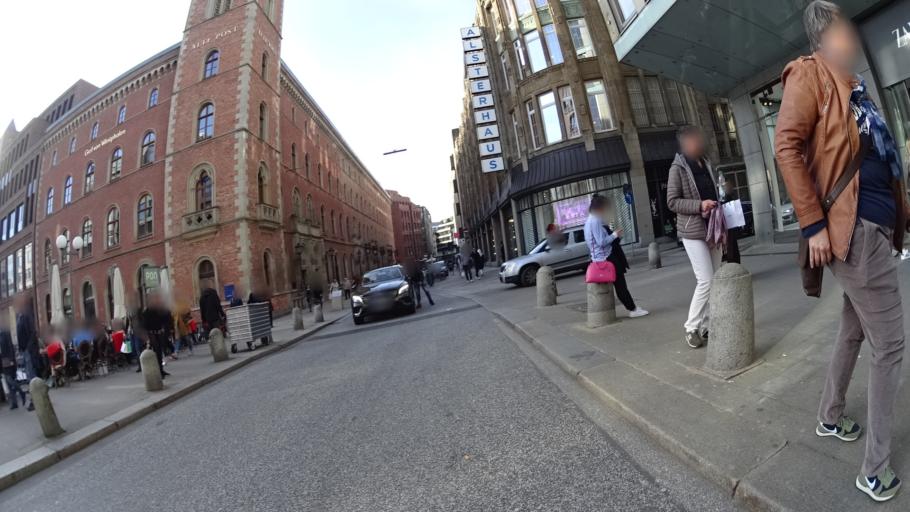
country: DE
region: Hamburg
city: Neustadt
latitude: 53.5526
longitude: 9.9910
